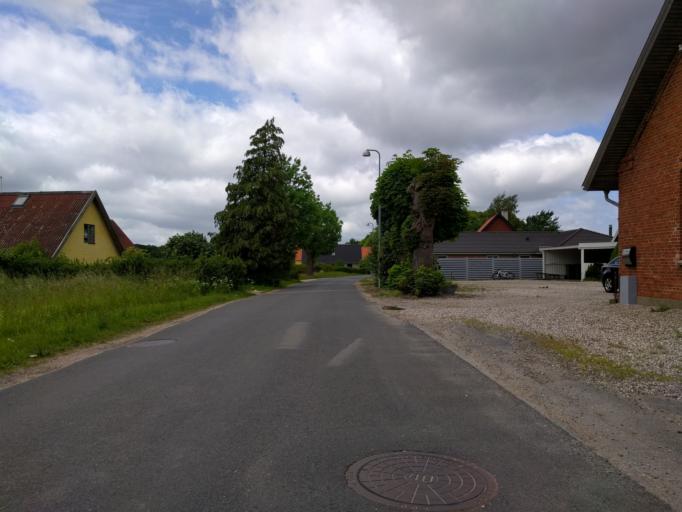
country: DK
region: South Denmark
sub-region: Odense Kommune
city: Bullerup
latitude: 55.4263
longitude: 10.4947
